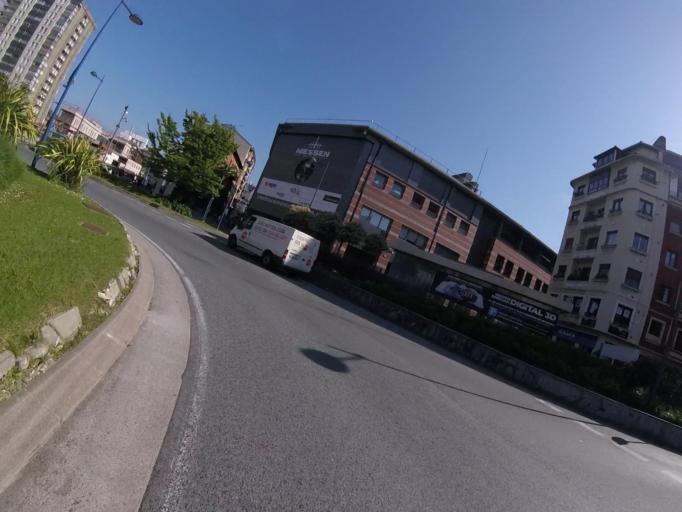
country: ES
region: Basque Country
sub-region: Provincia de Guipuzcoa
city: Errenteria
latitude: 43.3149
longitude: -1.9006
